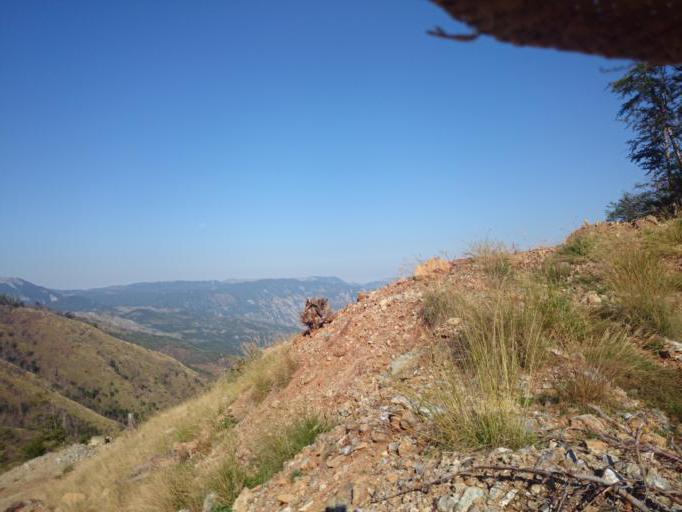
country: AL
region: Diber
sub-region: Rrethi i Bulqizes
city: Martanesh
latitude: 41.4042
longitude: 20.2993
